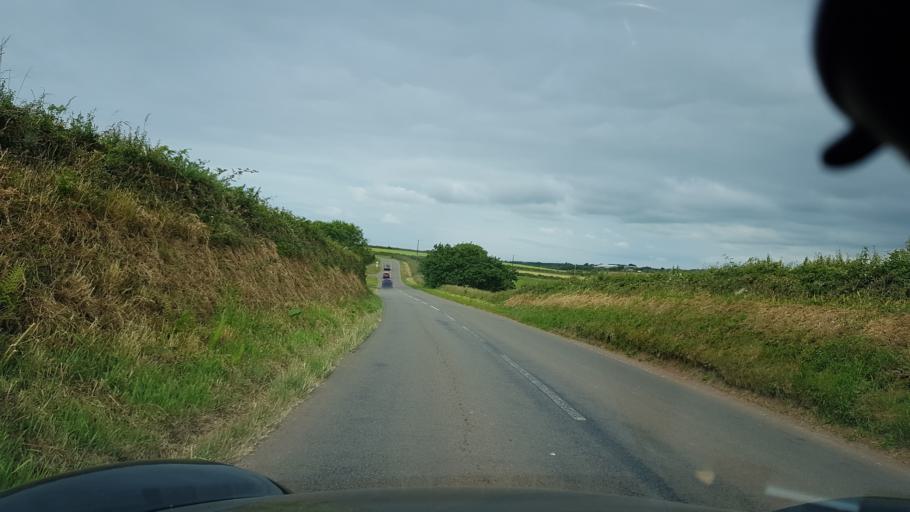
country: GB
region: Wales
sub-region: Pembrokeshire
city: Dale
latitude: 51.7474
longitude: -5.1436
